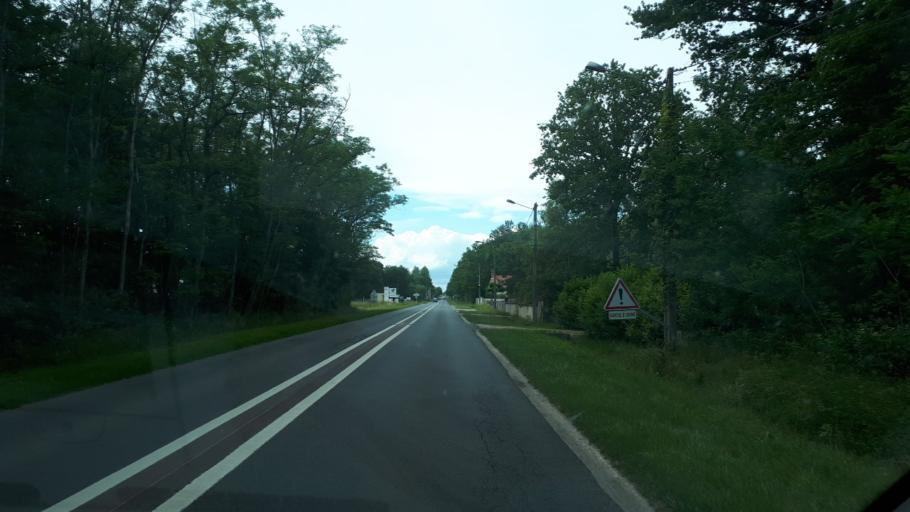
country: FR
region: Centre
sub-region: Departement du Loir-et-Cher
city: Villefranche-sur-Cher
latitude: 47.3069
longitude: 1.7660
